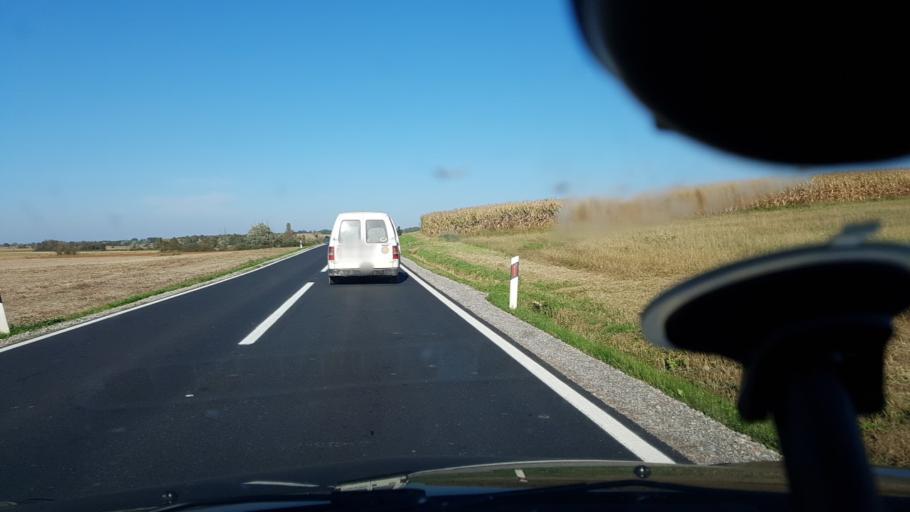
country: HR
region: Bjelovarsko-Bilogorska
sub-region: Grad Cazma
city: Cazma
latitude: 45.7915
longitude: 16.6886
